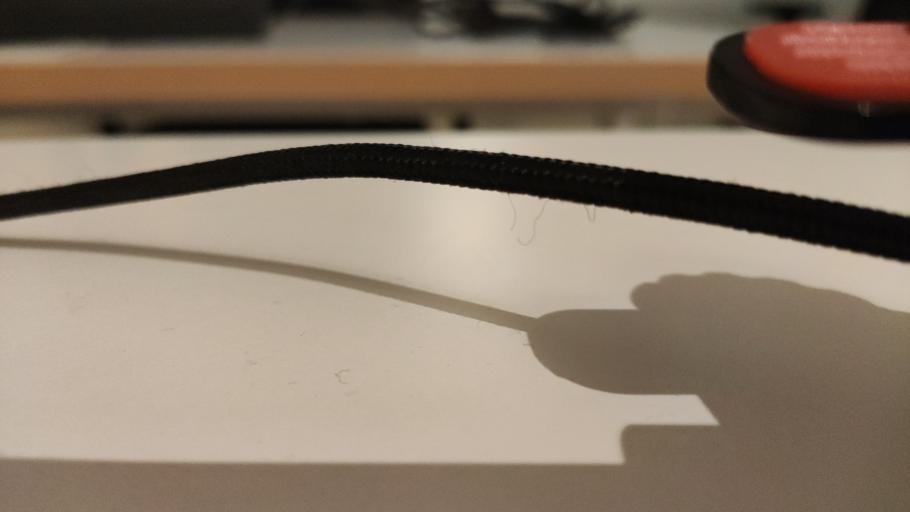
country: RU
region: Moskovskaya
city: Orekhovo-Zuyevo
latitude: 55.8235
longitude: 38.9649
